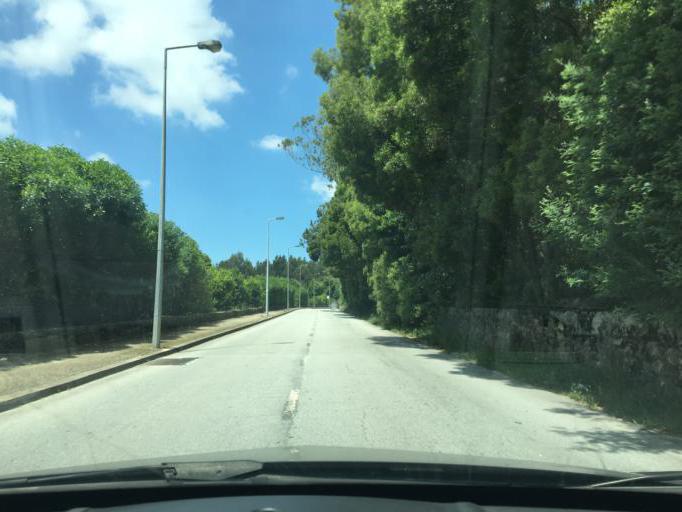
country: PT
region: Porto
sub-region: Maia
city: Anta
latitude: 41.2914
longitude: -8.6117
